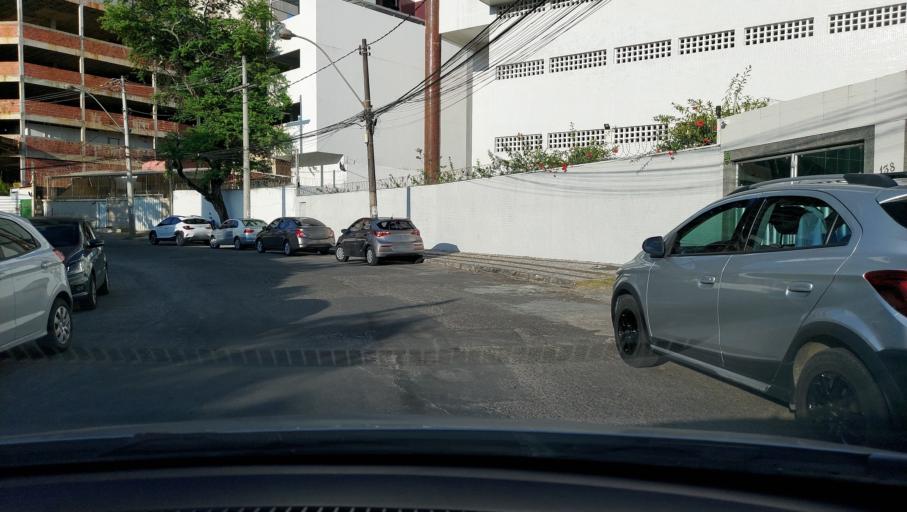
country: BR
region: Bahia
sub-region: Salvador
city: Salvador
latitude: -12.9882
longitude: -38.4554
